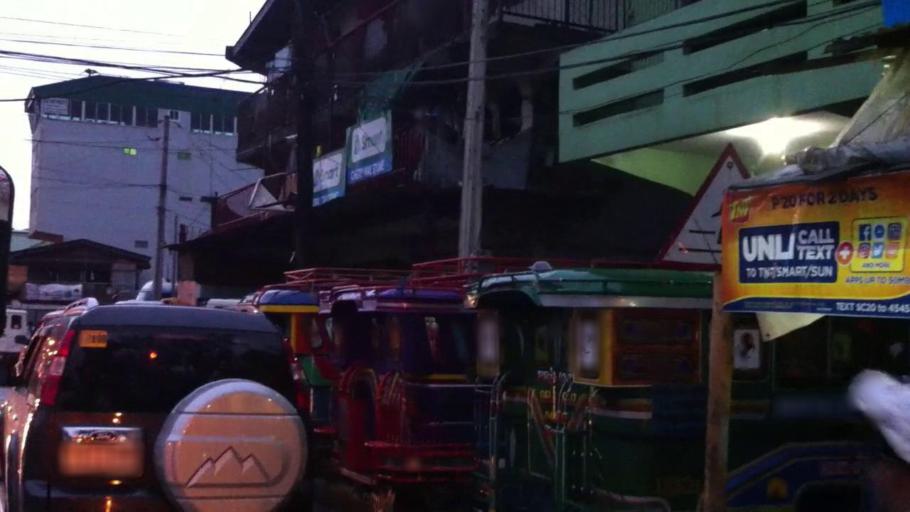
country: PH
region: Cordillera
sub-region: Province of Benguet
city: La Trinidad
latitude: 16.4452
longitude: 120.5841
